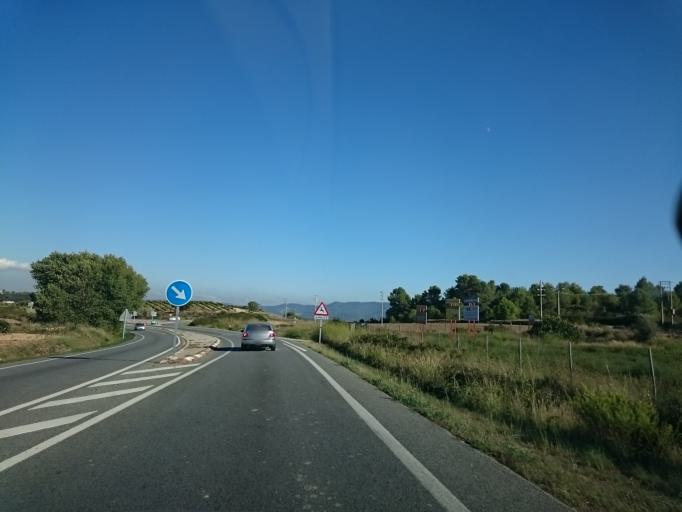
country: ES
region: Catalonia
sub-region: Provincia de Barcelona
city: Masquefa
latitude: 41.5028
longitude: 1.7856
